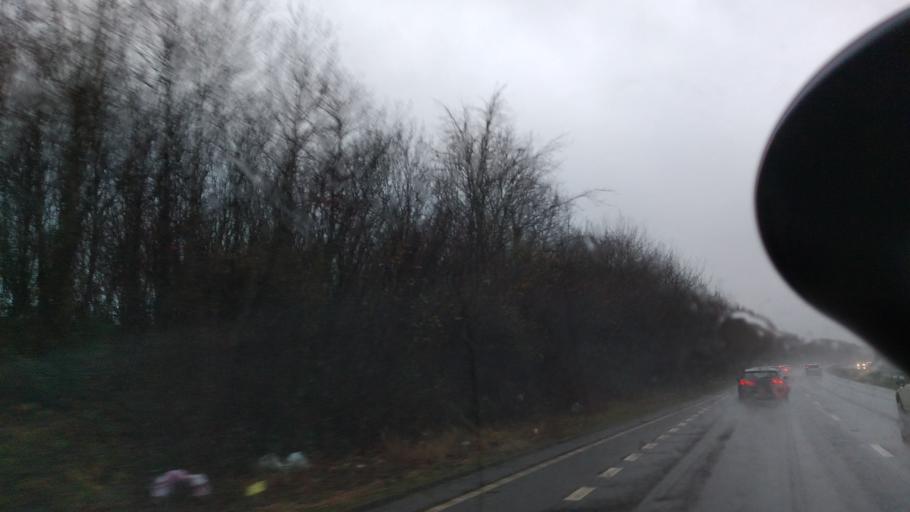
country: GB
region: England
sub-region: Brighton and Hove
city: Brighton
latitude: 50.8705
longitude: -0.1317
